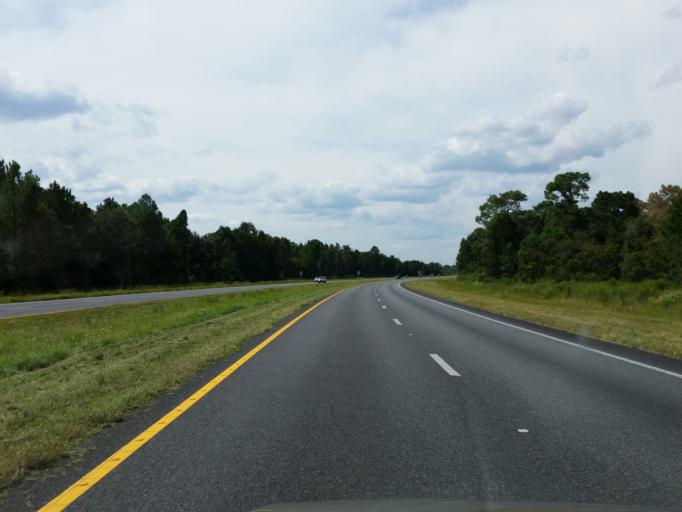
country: US
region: Florida
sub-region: Sumter County
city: Wildwood
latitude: 28.8497
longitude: -82.0631
